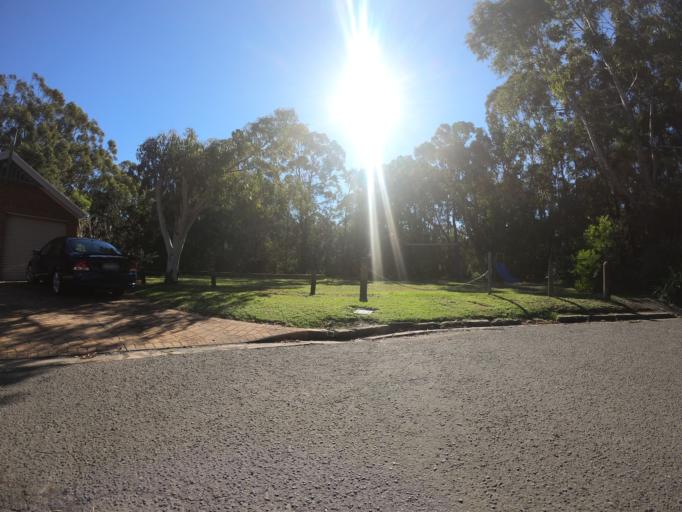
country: AU
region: New South Wales
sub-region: Wollongong
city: East Corrimal
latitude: -34.3810
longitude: 150.9092
